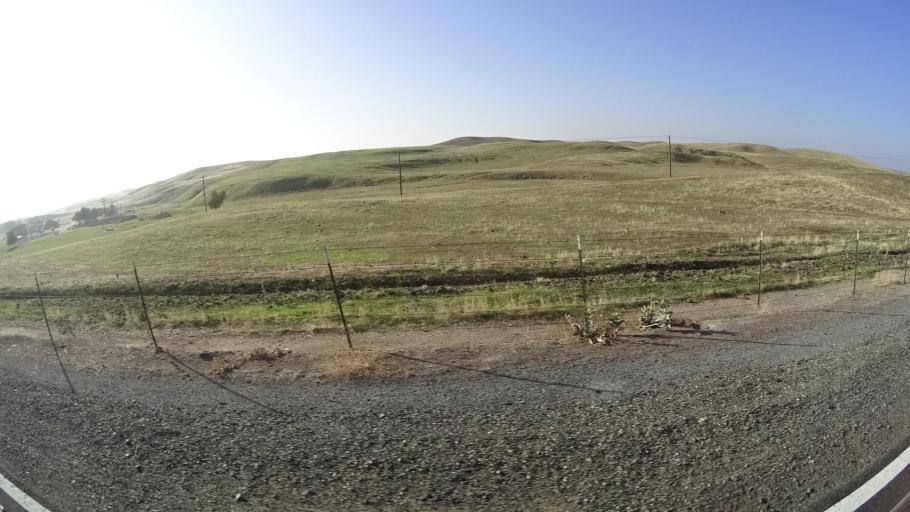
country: US
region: California
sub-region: Tulare County
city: Richgrove
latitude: 35.7400
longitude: -118.9595
